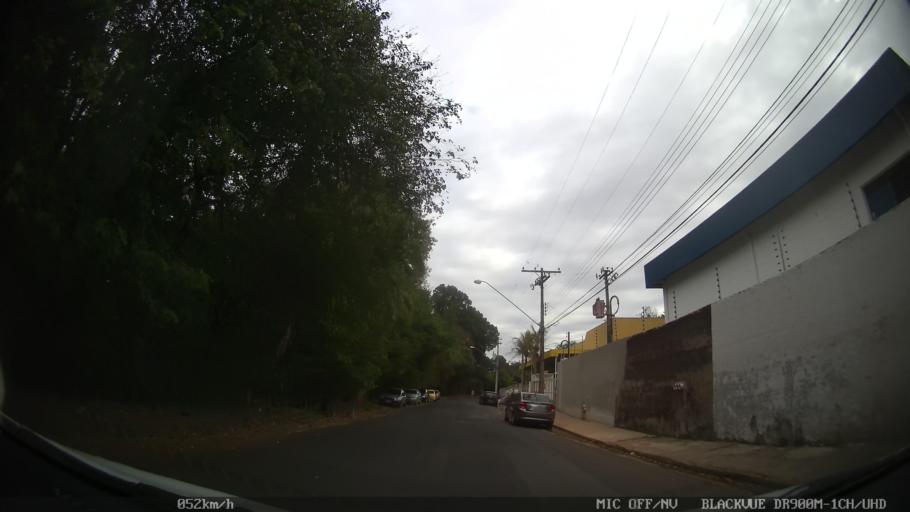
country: BR
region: Sao Paulo
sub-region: Sao Jose Do Rio Preto
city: Sao Jose do Rio Preto
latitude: -20.8192
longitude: -49.4305
